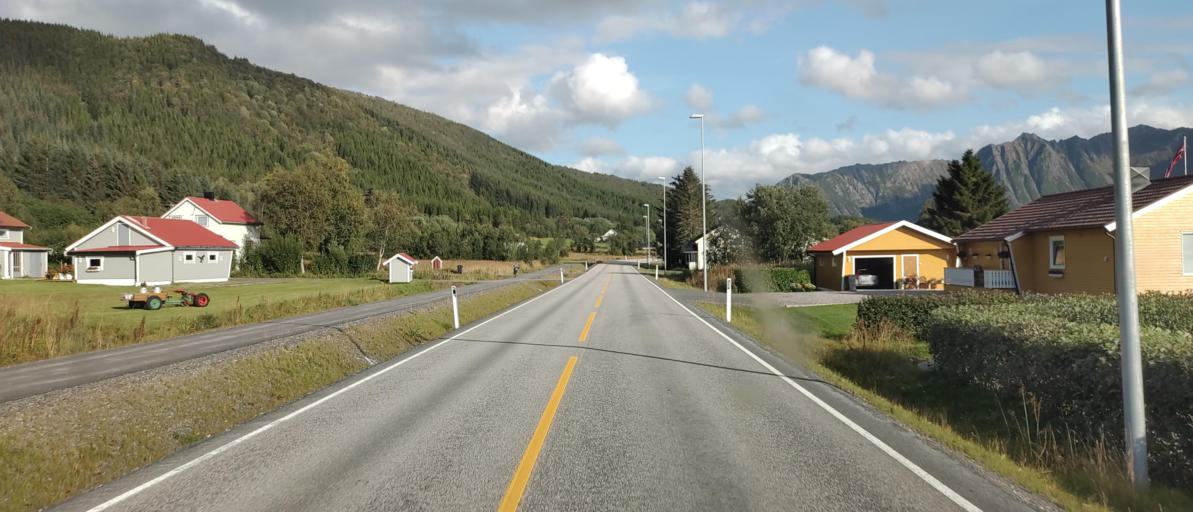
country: NO
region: Nordland
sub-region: Sortland
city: Sortland
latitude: 68.7511
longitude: 15.4853
